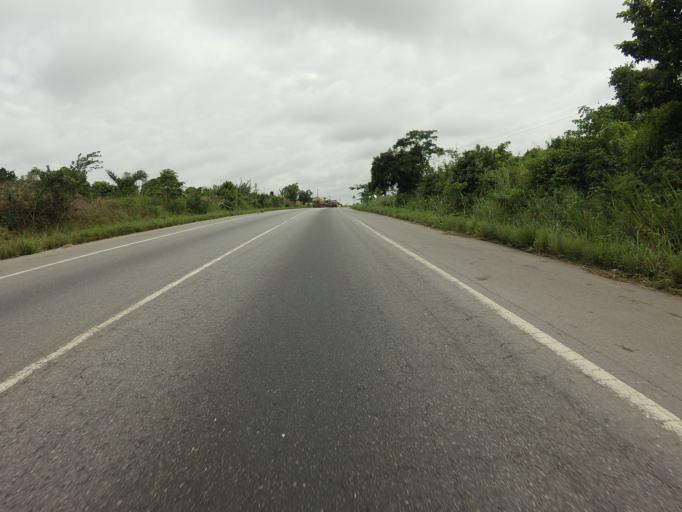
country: GH
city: Bechem
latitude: 7.0713
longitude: -1.7141
